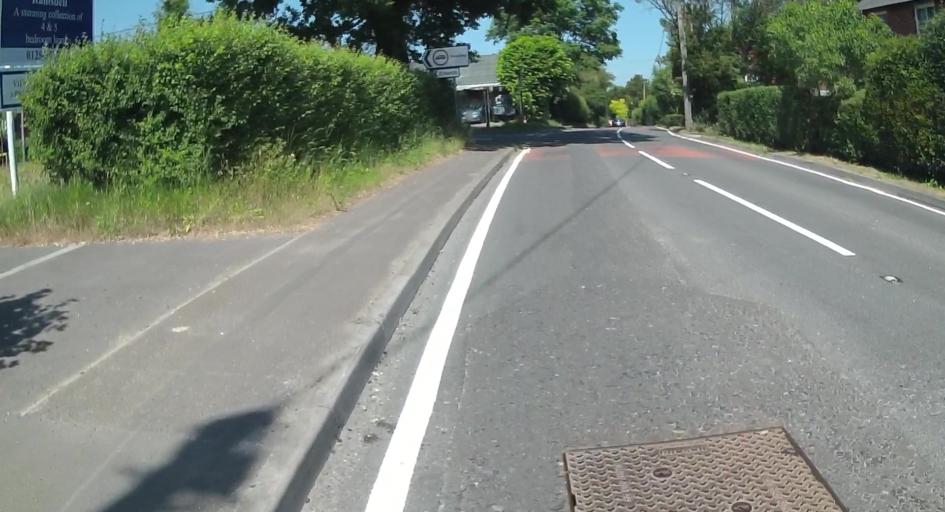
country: GB
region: England
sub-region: Hampshire
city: Kingsclere
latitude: 51.3534
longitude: -1.2039
